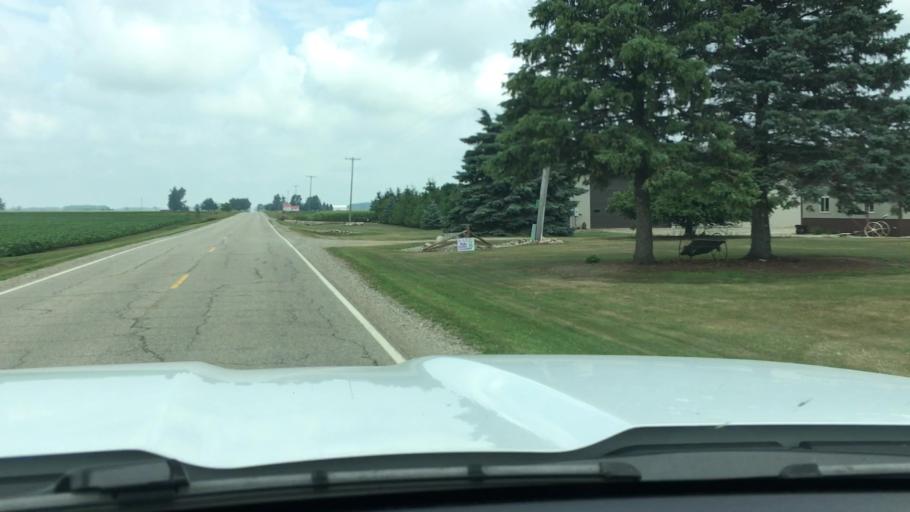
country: US
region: Michigan
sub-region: Sanilac County
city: Marlette
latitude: 43.3673
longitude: -83.0060
